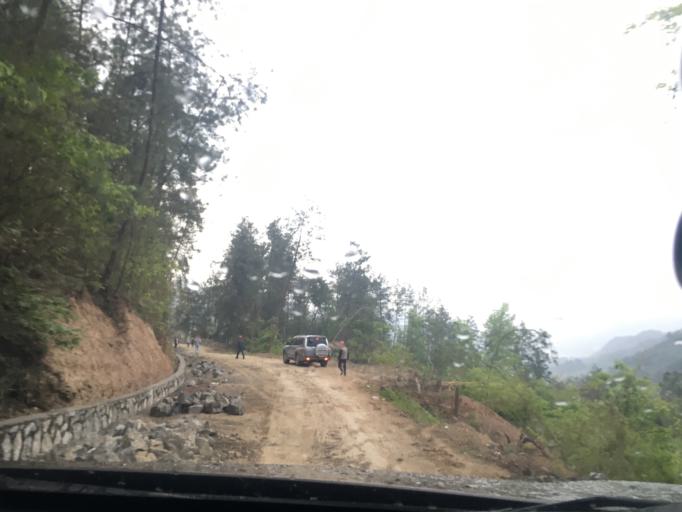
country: CN
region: Guizhou Sheng
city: Changbao
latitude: 28.2083
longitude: 108.2845
